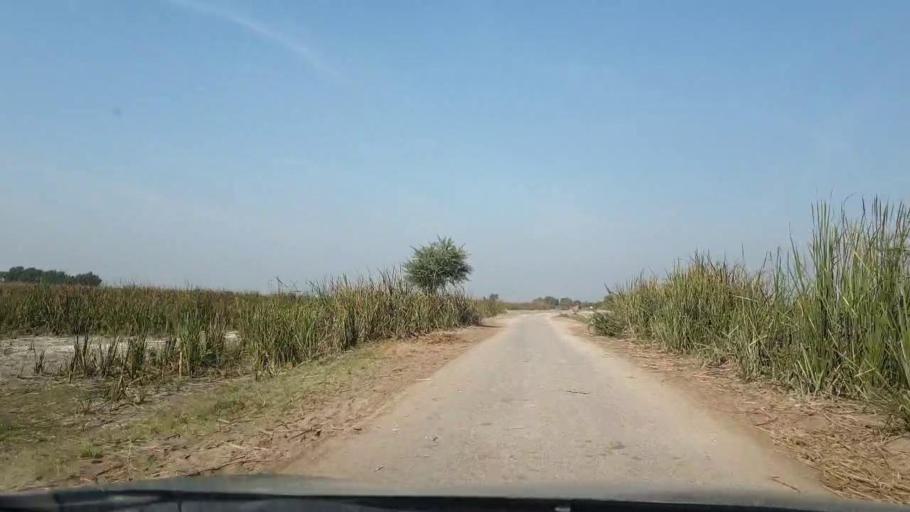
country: PK
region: Sindh
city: Berani
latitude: 25.6959
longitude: 68.7535
